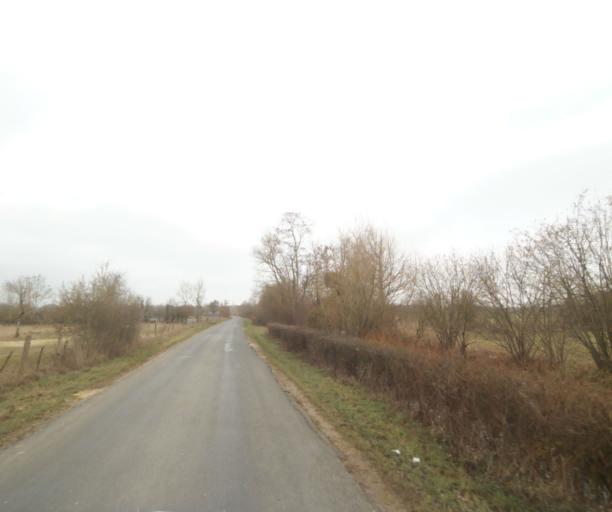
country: FR
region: Champagne-Ardenne
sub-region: Departement de la Haute-Marne
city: Villiers-en-Lieu
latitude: 48.6581
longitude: 4.8276
